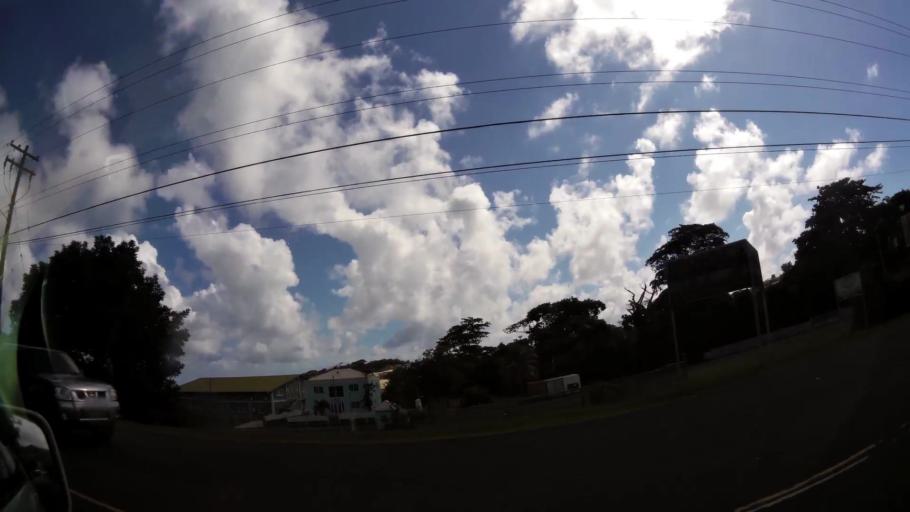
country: VC
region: Saint George
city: Kingstown
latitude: 13.1437
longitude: -61.1709
